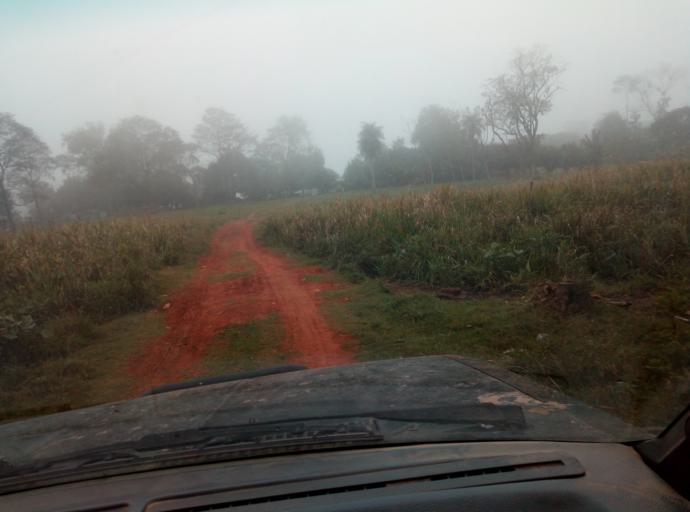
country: PY
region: Caaguazu
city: Doctor Cecilio Baez
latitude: -25.1550
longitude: -56.2495
